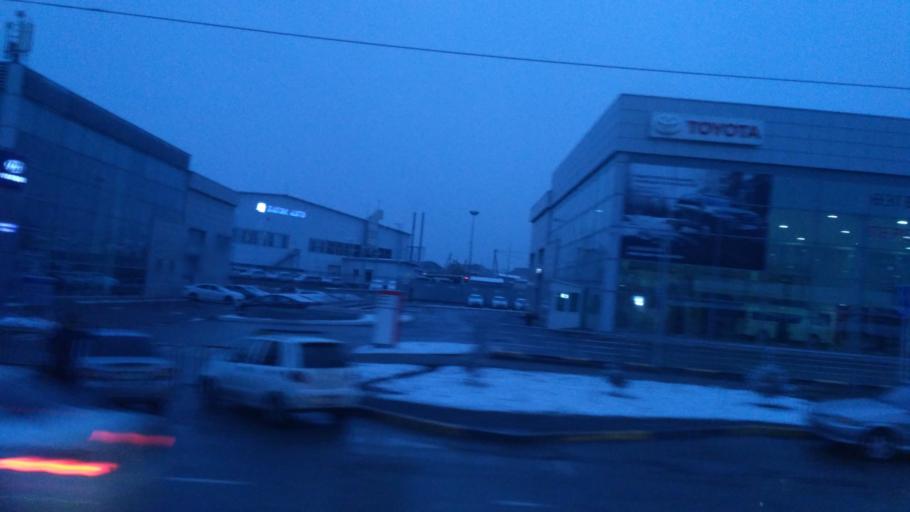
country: KZ
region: Ongtustik Qazaqstan
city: Shymkent
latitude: 42.3513
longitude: 69.5319
